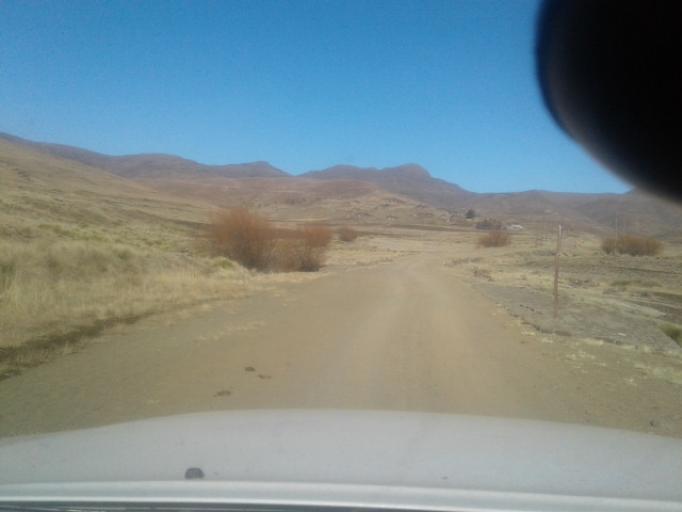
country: LS
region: Maseru
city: Nako
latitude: -29.3770
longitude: 28.0178
